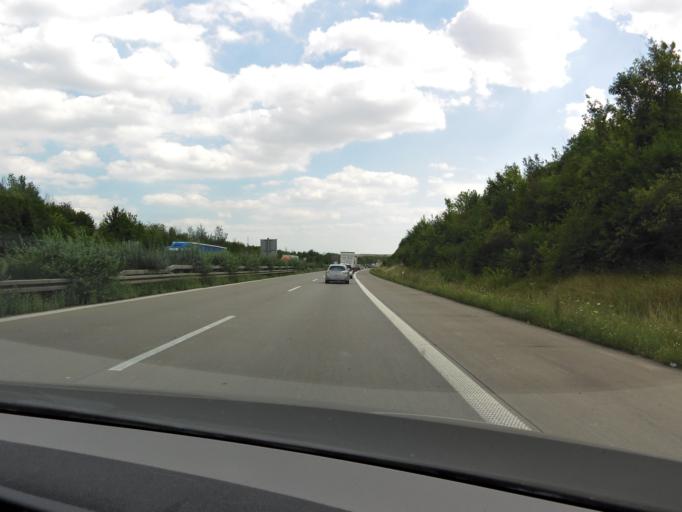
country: DE
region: Saxony-Anhalt
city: Welsleben
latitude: 52.0506
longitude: 11.6216
